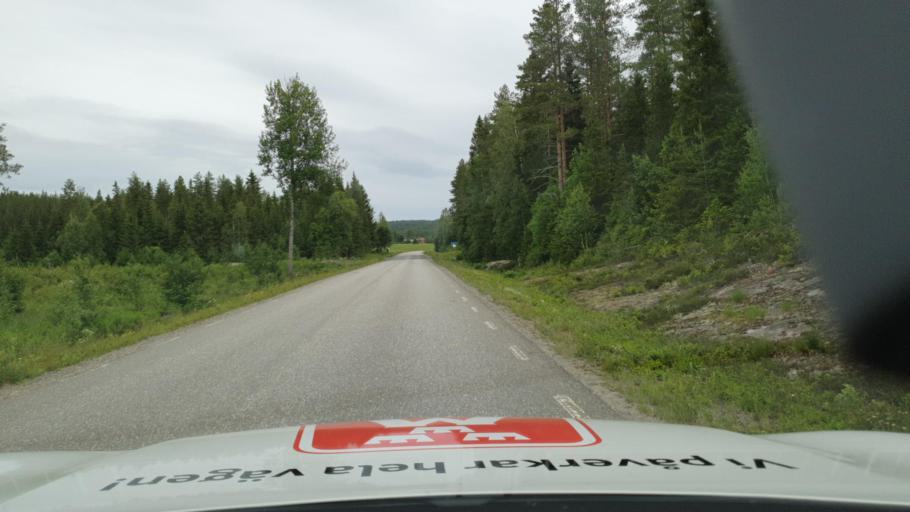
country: SE
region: Vaesterbotten
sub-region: Skelleftea Kommun
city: Burtraesk
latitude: 64.3008
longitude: 20.6485
